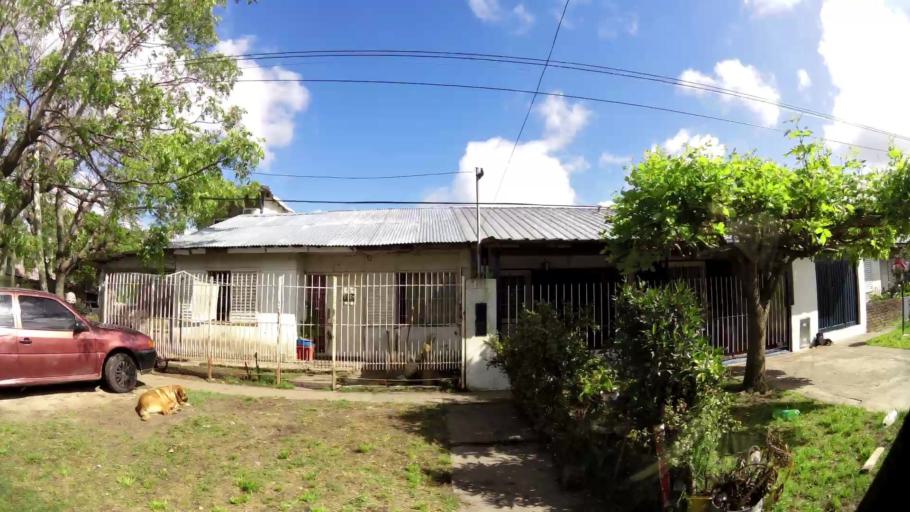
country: AR
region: Buenos Aires
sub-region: Partido de Quilmes
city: Quilmes
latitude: -34.7975
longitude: -58.1584
